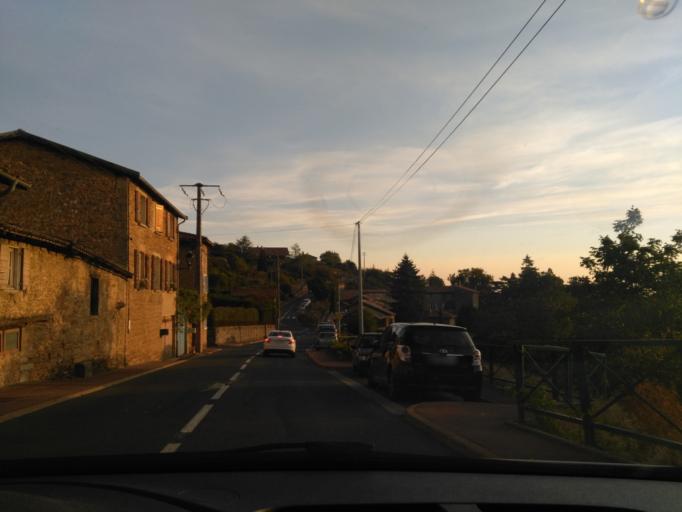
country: FR
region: Rhone-Alpes
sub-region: Departement du Rhone
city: Limonest
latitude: 45.8516
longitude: 4.7956
